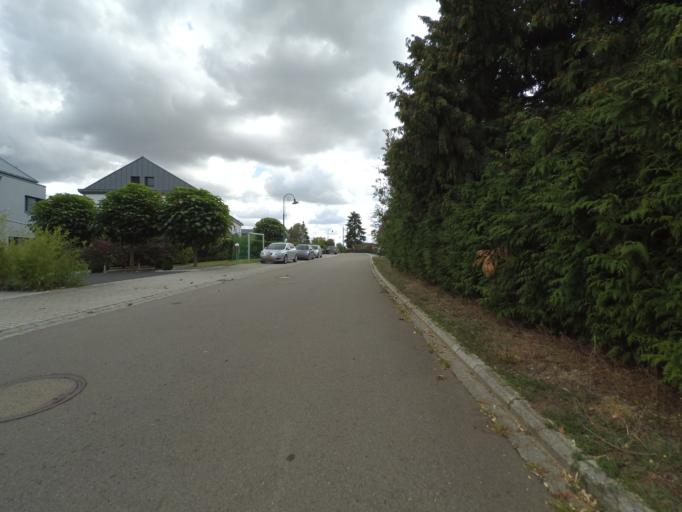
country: LU
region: Luxembourg
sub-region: Canton de Luxembourg
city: Weiler-la-Tour
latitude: 49.5559
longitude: 6.2063
